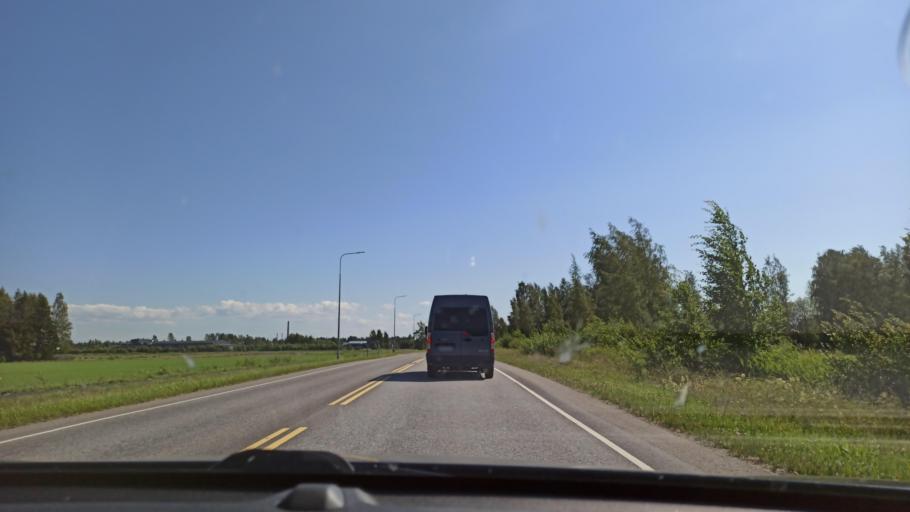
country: FI
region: Satakunta
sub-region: Pori
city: Pori
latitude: 61.5171
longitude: 21.8034
